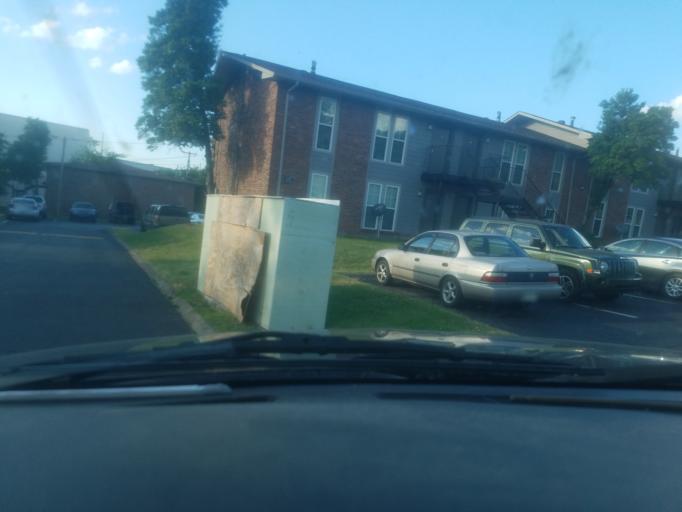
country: US
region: Tennessee
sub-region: Davidson County
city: Nashville
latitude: 36.1610
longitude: -86.8442
